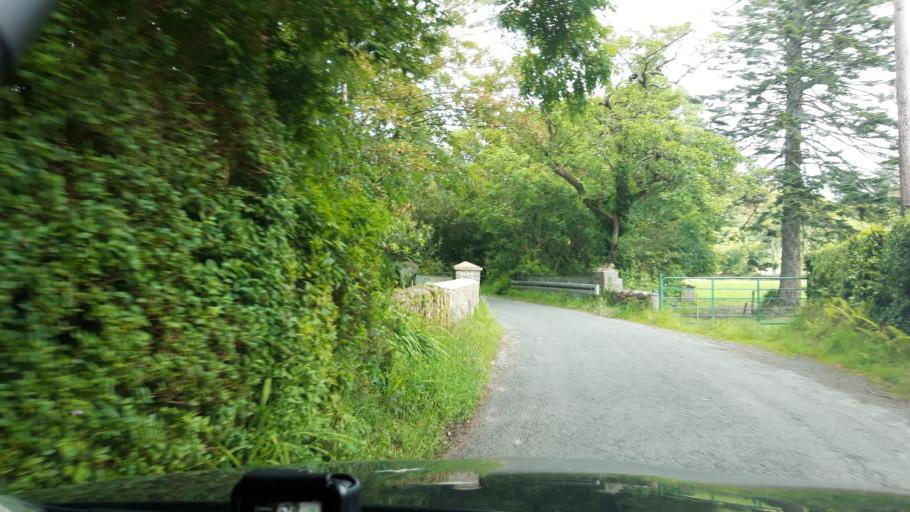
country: IE
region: Leinster
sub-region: Loch Garman
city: Loch Garman
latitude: 52.2844
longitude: -6.5004
